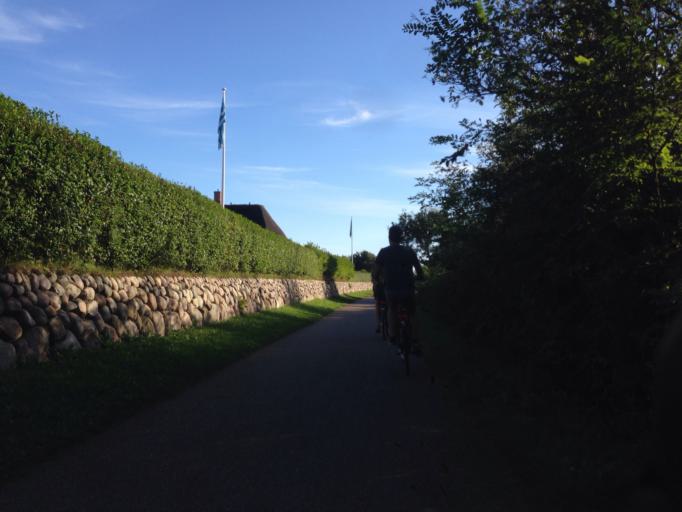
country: DE
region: Schleswig-Holstein
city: Tinnum
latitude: 54.9494
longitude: 8.3364
